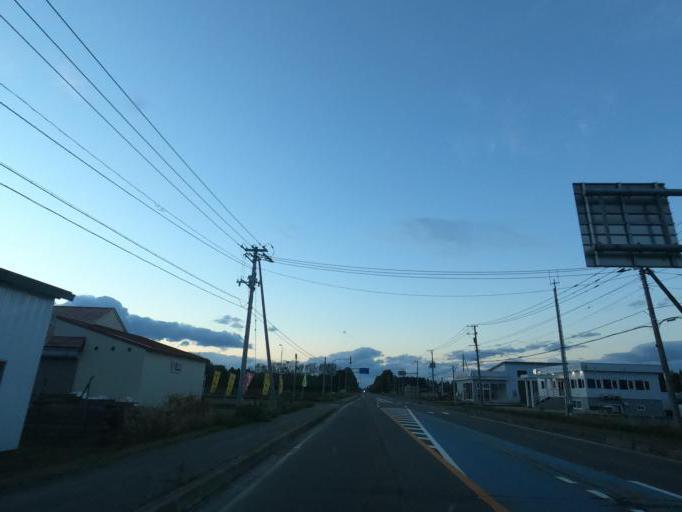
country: JP
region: Hokkaido
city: Obihiro
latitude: 42.6539
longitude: 143.1891
